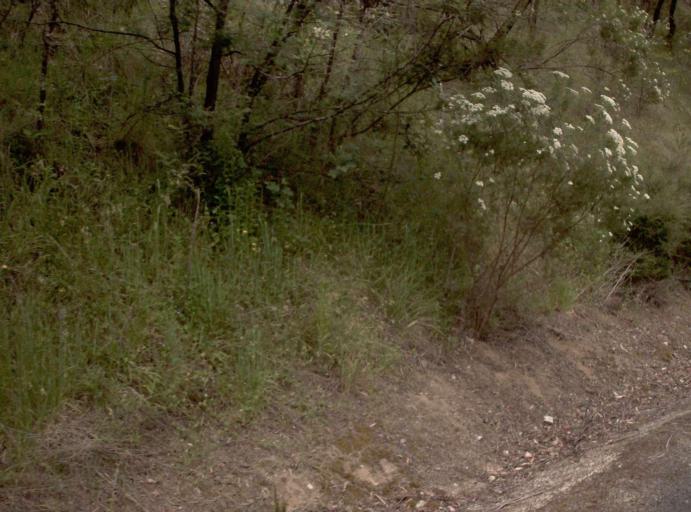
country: AU
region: New South Wales
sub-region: Bombala
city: Bombala
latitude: -37.3592
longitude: 149.2003
